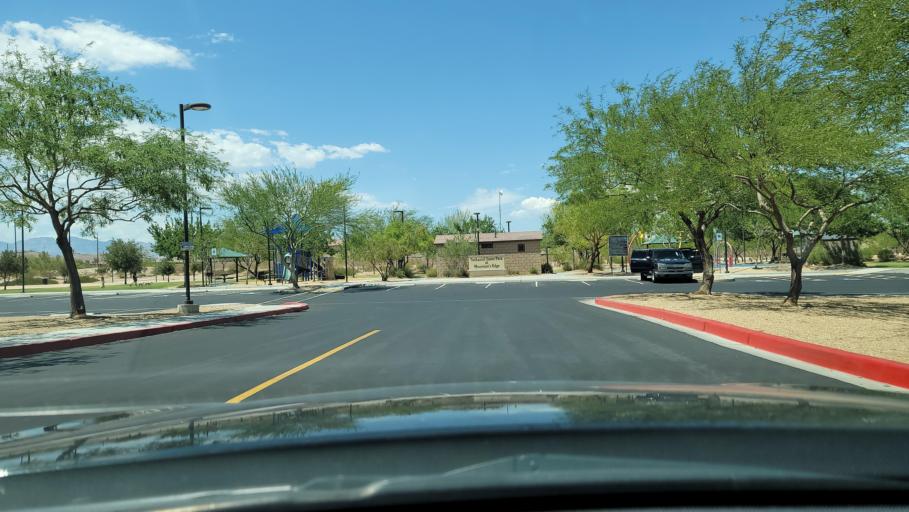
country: US
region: Nevada
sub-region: Clark County
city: Enterprise
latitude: 36.0062
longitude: -115.2845
